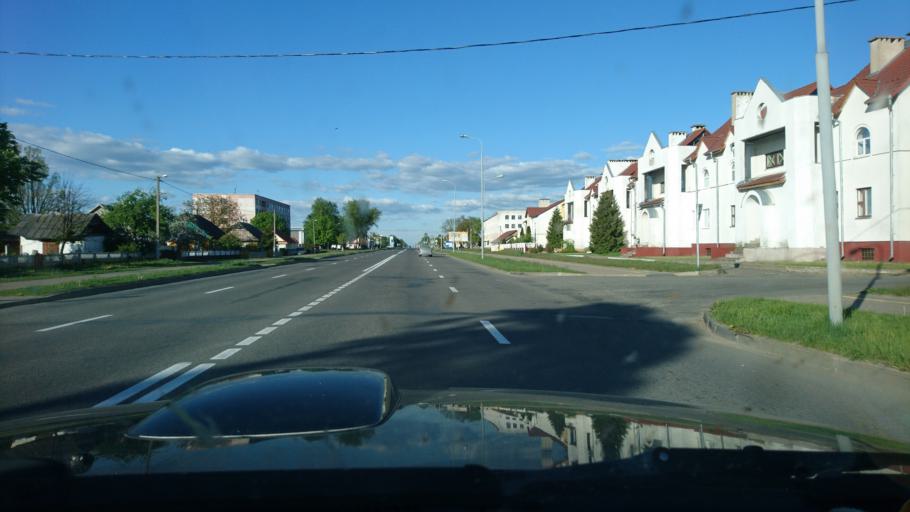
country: BY
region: Brest
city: Ivatsevichy
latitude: 52.7042
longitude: 25.3277
